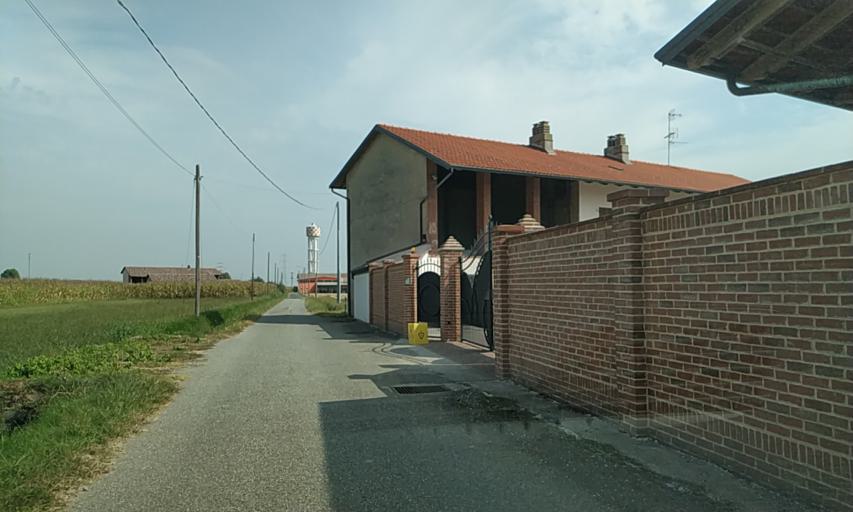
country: IT
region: Piedmont
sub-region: Provincia di Vercelli
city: Livorno Ferraris
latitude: 45.3150
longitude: 8.0692
